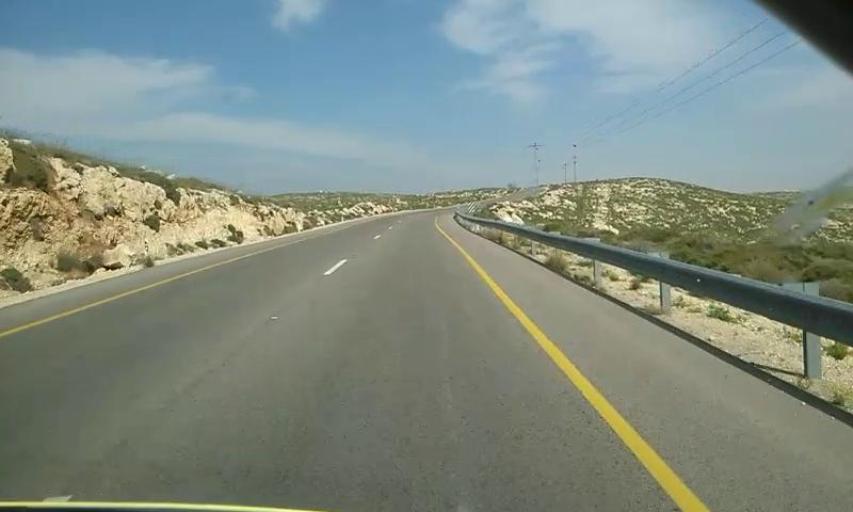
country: PS
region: West Bank
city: As Samu`
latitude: 31.3940
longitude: 35.0211
